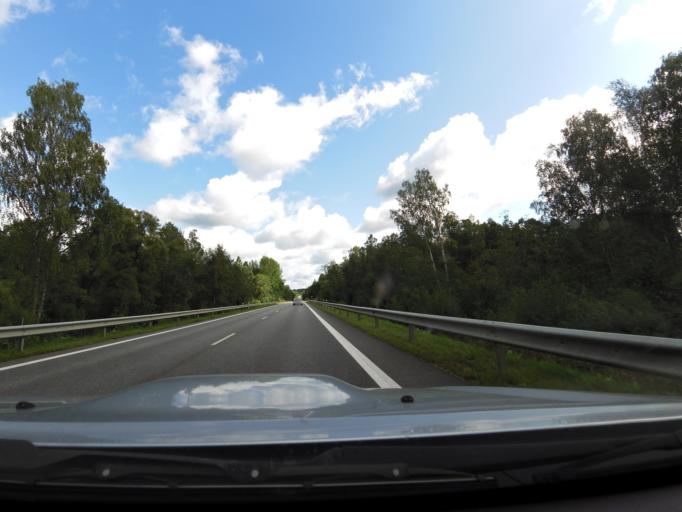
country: LT
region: Utenos apskritis
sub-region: Utena
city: Utena
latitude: 55.5742
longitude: 25.7847
